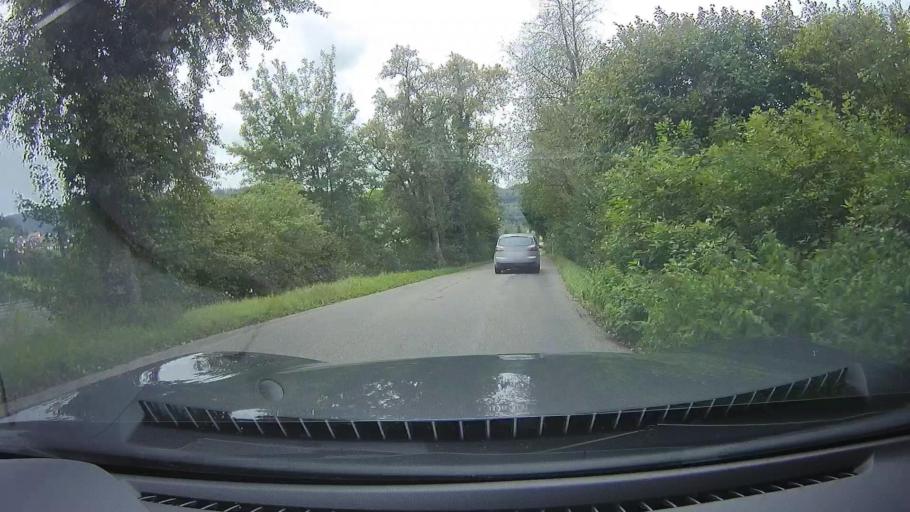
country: DE
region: Baden-Wuerttemberg
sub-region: Regierungsbezirk Stuttgart
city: Murrhardt
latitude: 48.9877
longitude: 9.5824
